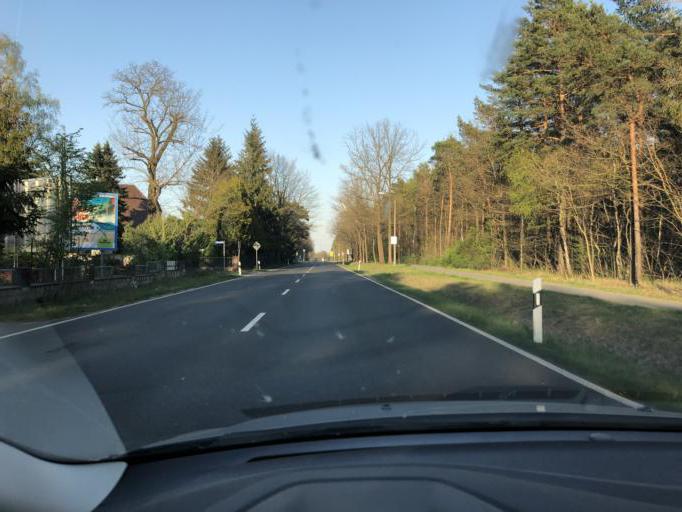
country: DE
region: Brandenburg
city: Schwarzbach
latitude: 51.4778
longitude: 13.9077
